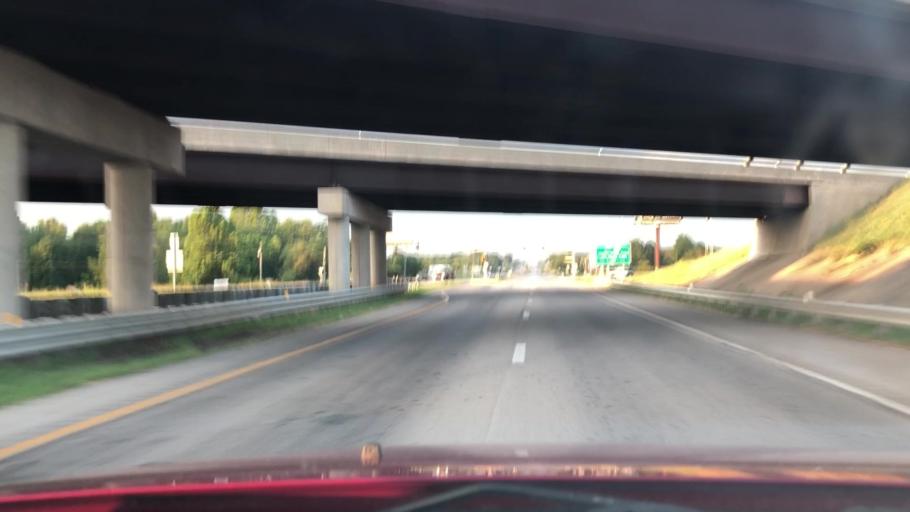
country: US
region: Missouri
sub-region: Greene County
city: Battlefield
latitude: 37.1613
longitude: -93.3992
